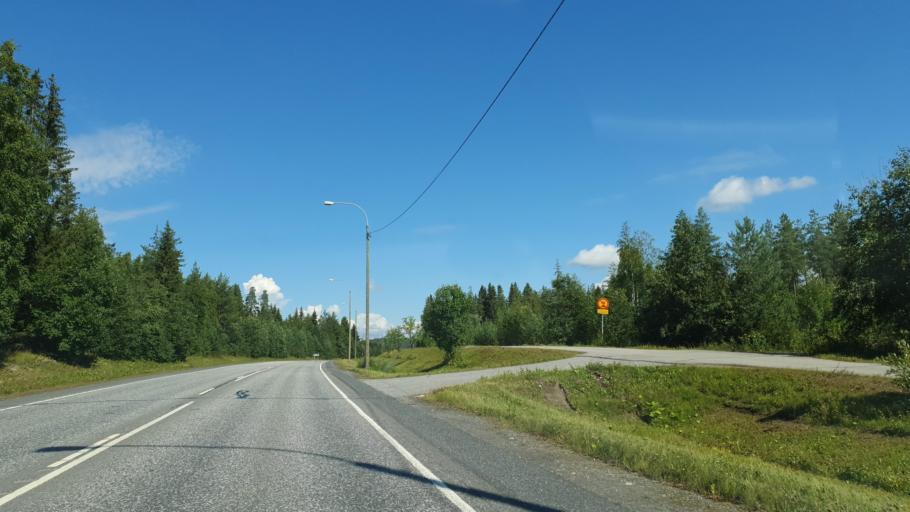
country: FI
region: Northern Savo
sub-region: Ylae-Savo
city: Iisalmi
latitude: 63.6318
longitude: 27.2253
